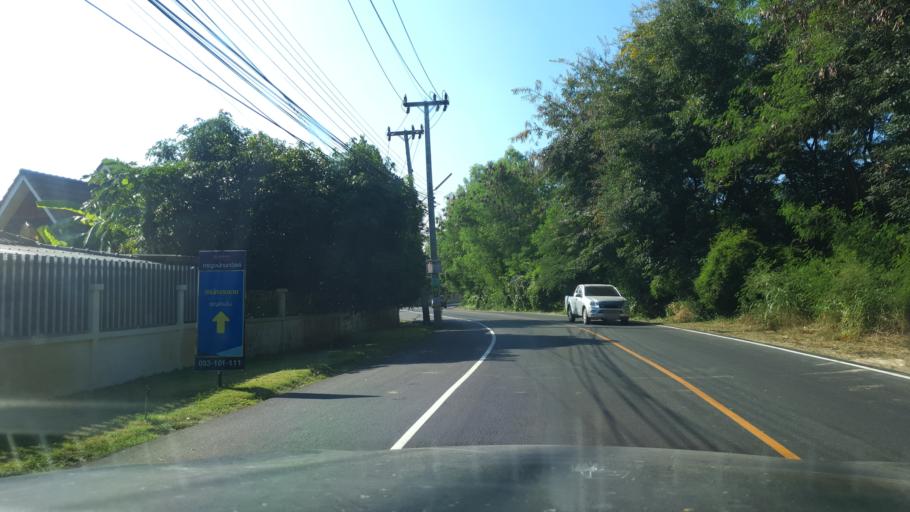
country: TH
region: Chiang Mai
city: San Kamphaeng
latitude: 18.7379
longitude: 99.0747
